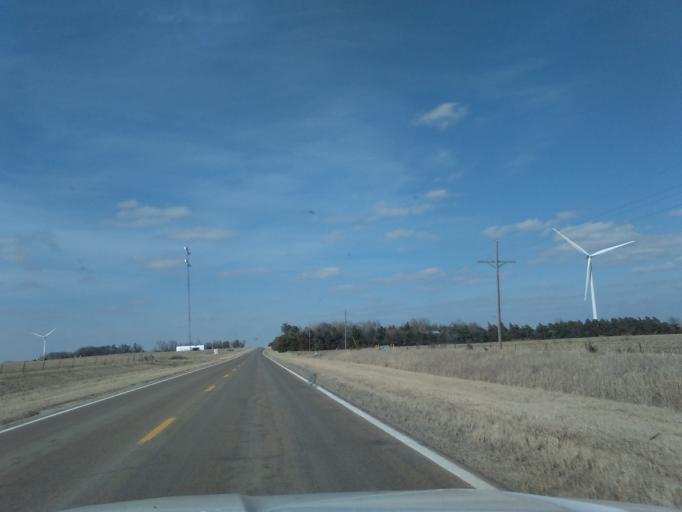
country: US
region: Kansas
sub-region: Washington County
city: Washington
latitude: 40.0506
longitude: -96.9351
